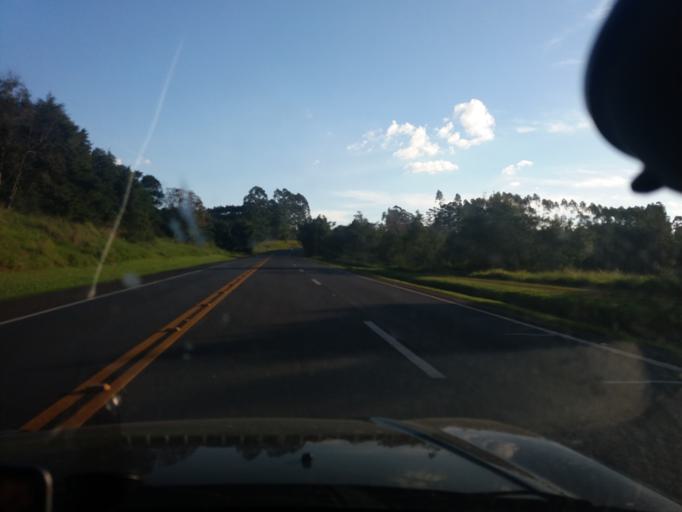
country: BR
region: Sao Paulo
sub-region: Buri
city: Buri
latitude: -23.9279
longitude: -48.6635
